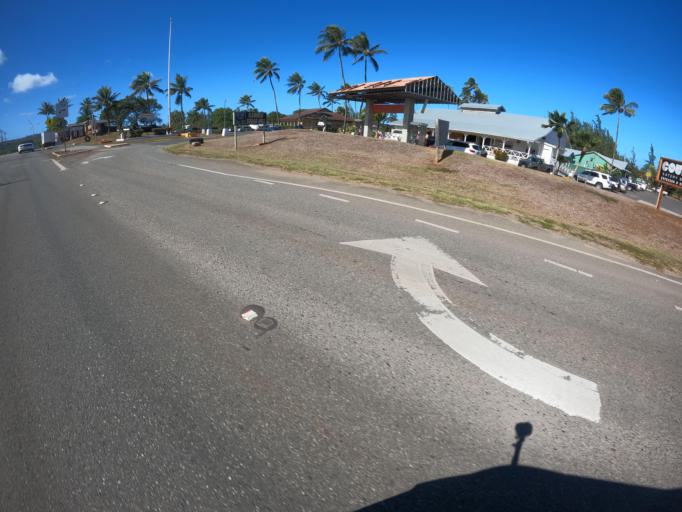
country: US
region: Hawaii
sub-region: Honolulu County
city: Kahuku
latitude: 21.6775
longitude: -157.9502
